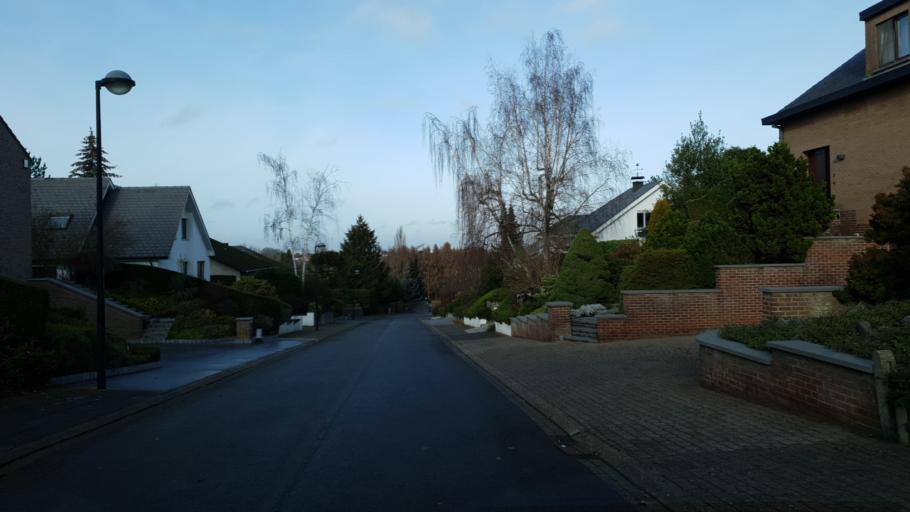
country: BE
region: Flanders
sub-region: Provincie Vlaams-Brabant
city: Kortenberg
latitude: 50.8734
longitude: 4.5369
